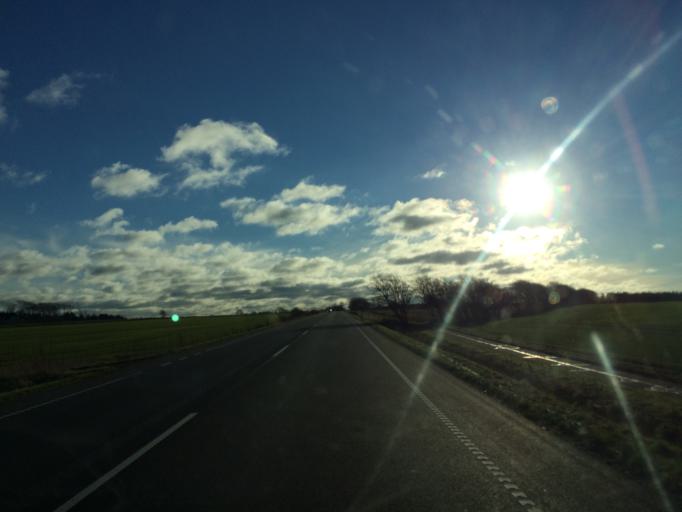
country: DK
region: Central Jutland
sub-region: Herning Kommune
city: Kibaek
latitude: 56.0211
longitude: 8.8517
